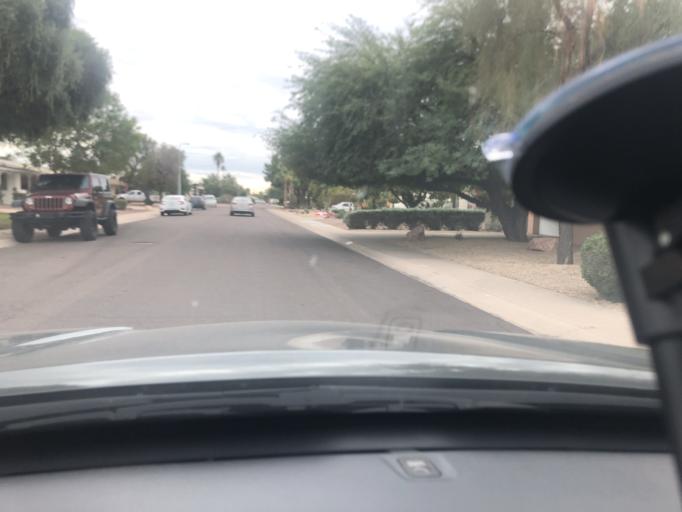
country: US
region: Arizona
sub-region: Maricopa County
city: Scottsdale
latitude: 33.4830
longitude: -111.9053
